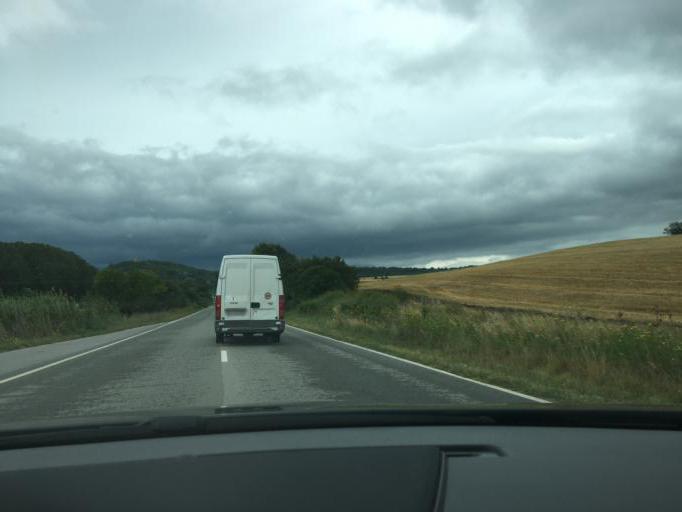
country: BG
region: Kyustendil
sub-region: Obshtina Bobovdol
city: Bobovdol
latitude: 42.2736
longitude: 22.9823
